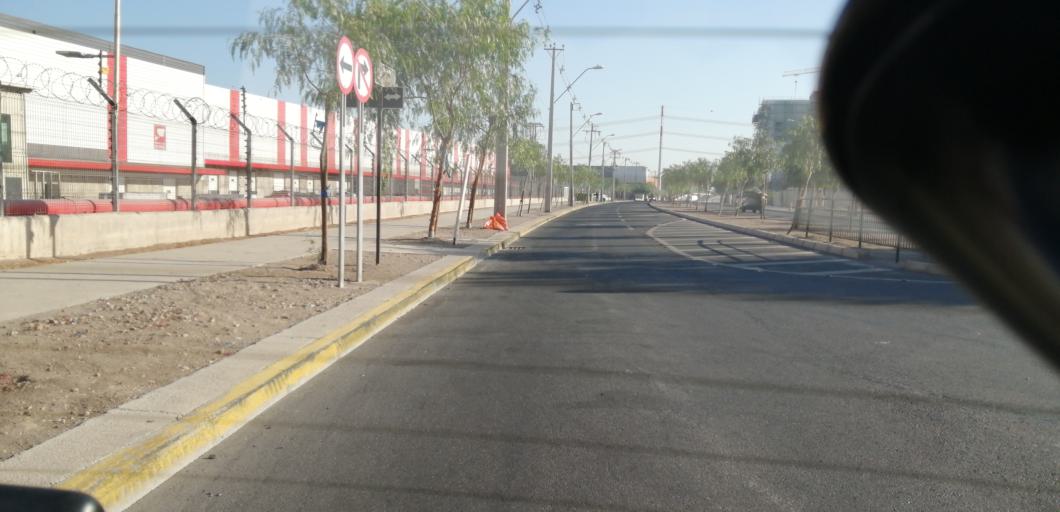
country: CL
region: Santiago Metropolitan
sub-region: Provincia de Santiago
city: Lo Prado
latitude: -33.4351
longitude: -70.7882
